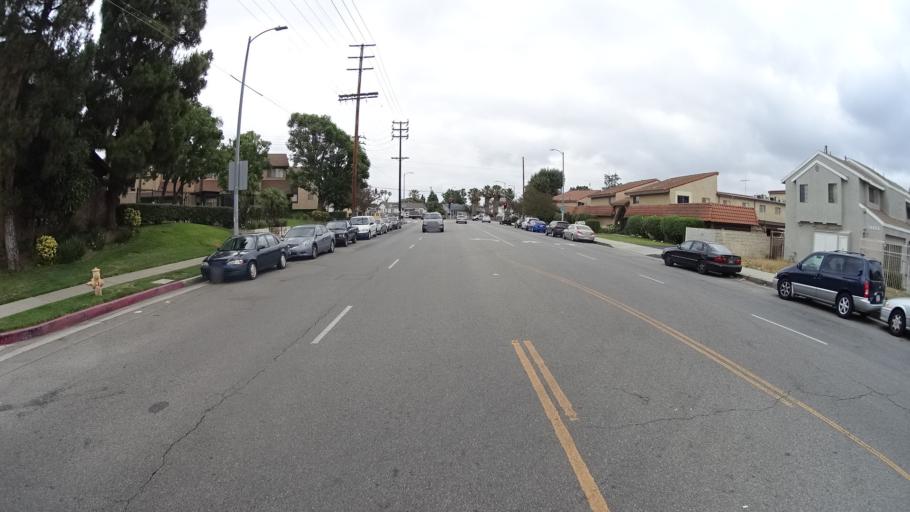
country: US
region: California
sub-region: Los Angeles County
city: San Fernando
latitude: 34.2427
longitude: -118.4465
